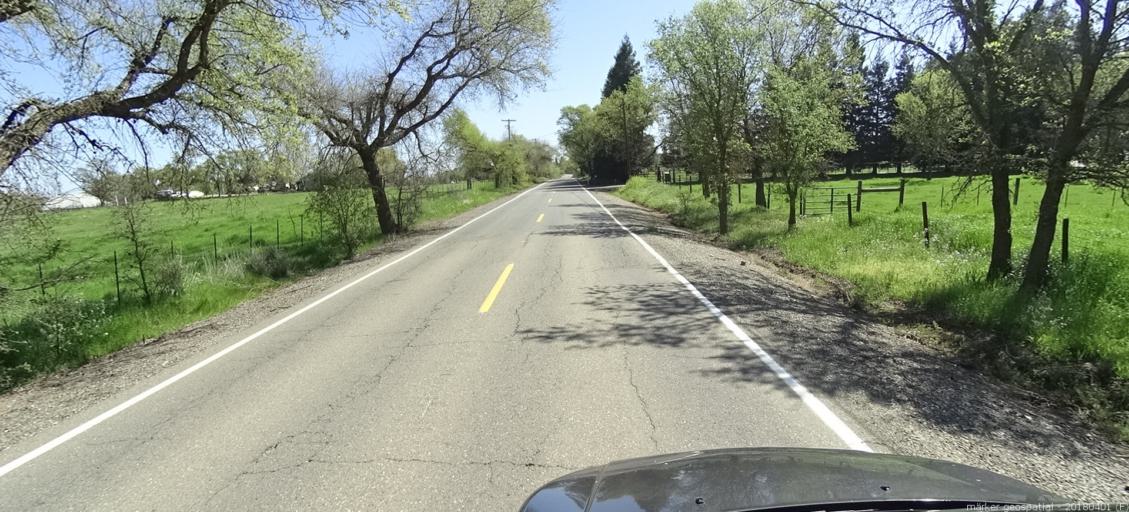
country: US
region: California
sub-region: Sacramento County
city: Wilton
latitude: 38.4184
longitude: -121.2389
